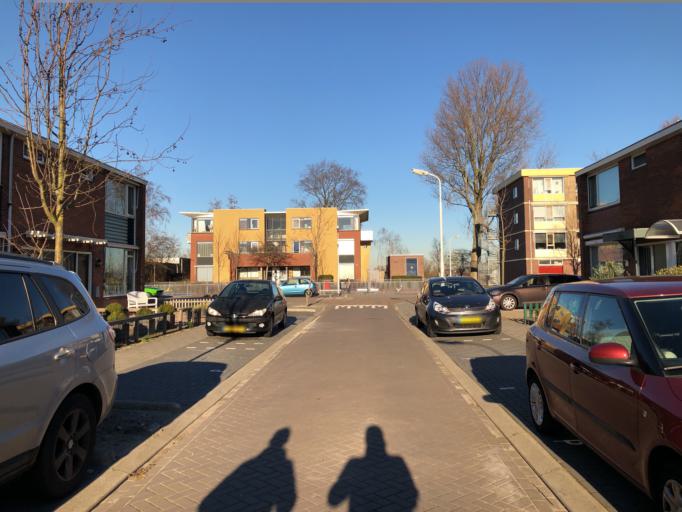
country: NL
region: North Holland
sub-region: Gemeente Uitgeest
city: Uitgeest
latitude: 52.5078
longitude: 4.7615
